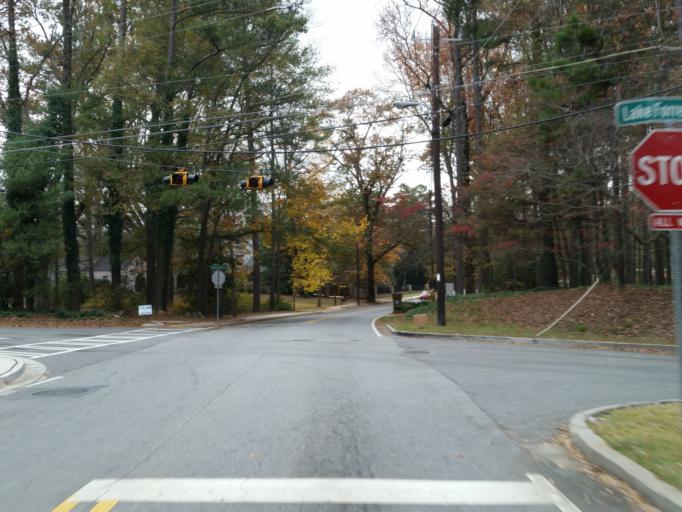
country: US
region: Georgia
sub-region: Fulton County
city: Sandy Springs
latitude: 33.8945
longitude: -84.3870
